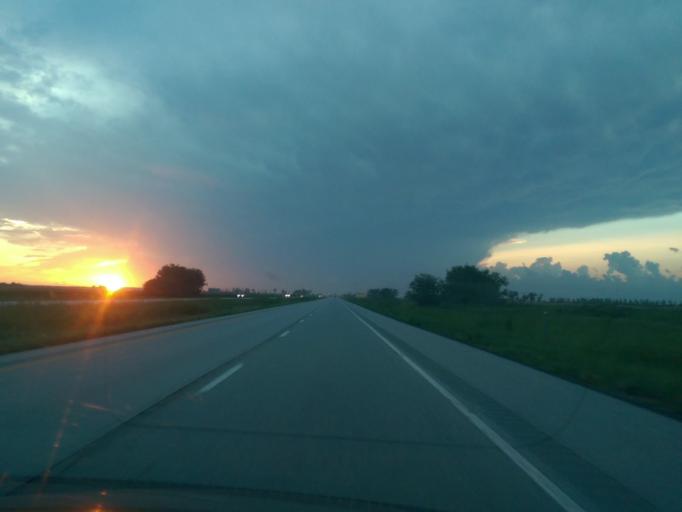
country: US
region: Iowa
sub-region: Fremont County
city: Hamburg
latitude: 40.6086
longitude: -95.6853
